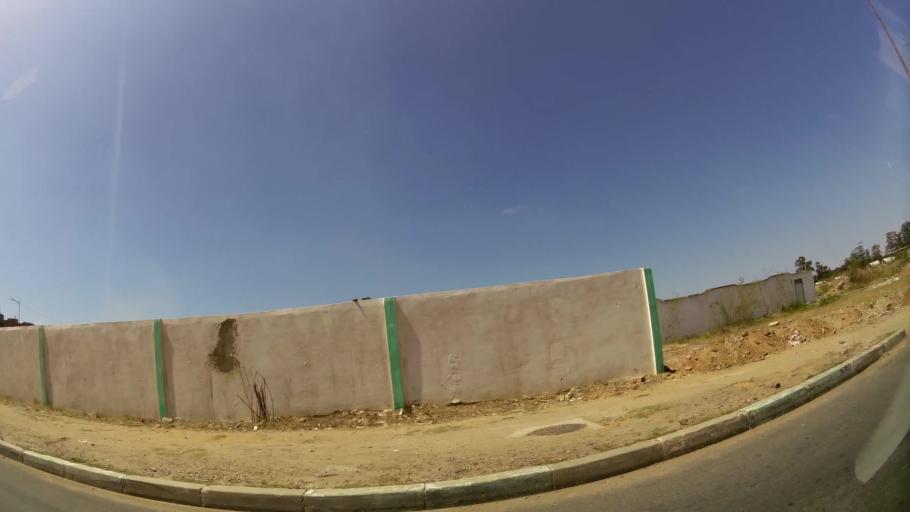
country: MA
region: Gharb-Chrarda-Beni Hssen
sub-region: Kenitra Province
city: Kenitra
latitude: 34.2500
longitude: -6.5380
